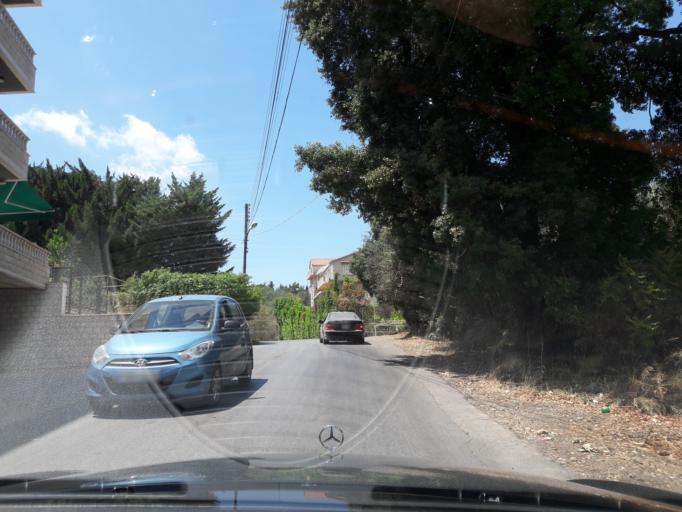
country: LB
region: Mont-Liban
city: Djounie
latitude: 33.9256
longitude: 35.6675
